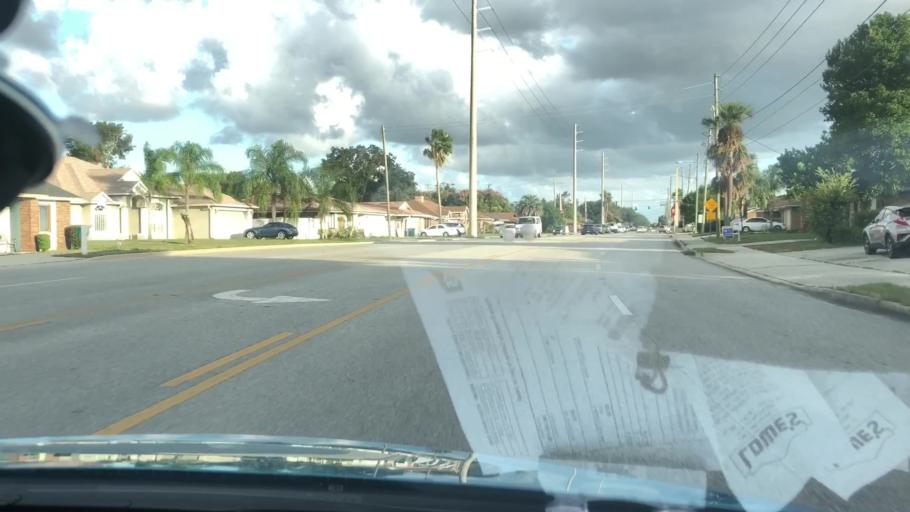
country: US
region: Florida
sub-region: Volusia County
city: Deltona
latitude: 28.9019
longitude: -81.2417
